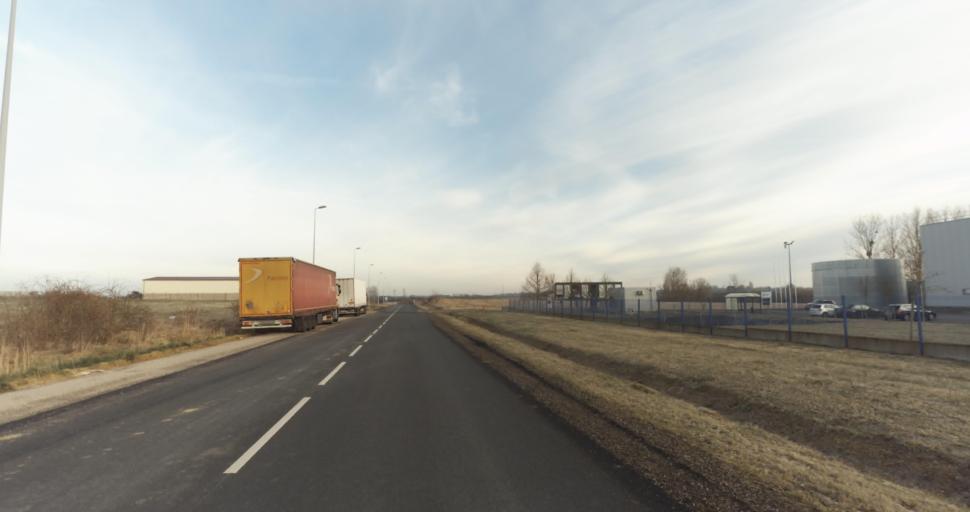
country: FR
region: Lorraine
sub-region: Departement de Meurthe-et-Moselle
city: Giraumont
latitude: 49.1563
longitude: 5.9038
